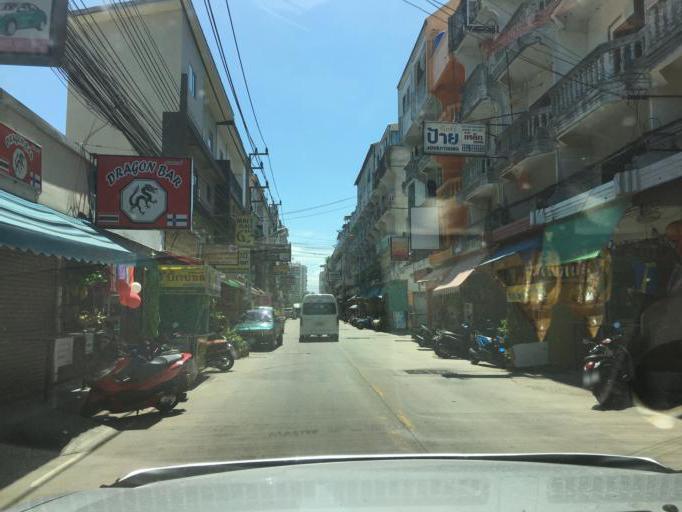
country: TH
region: Chon Buri
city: Phatthaya
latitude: 12.8869
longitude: 100.8797
